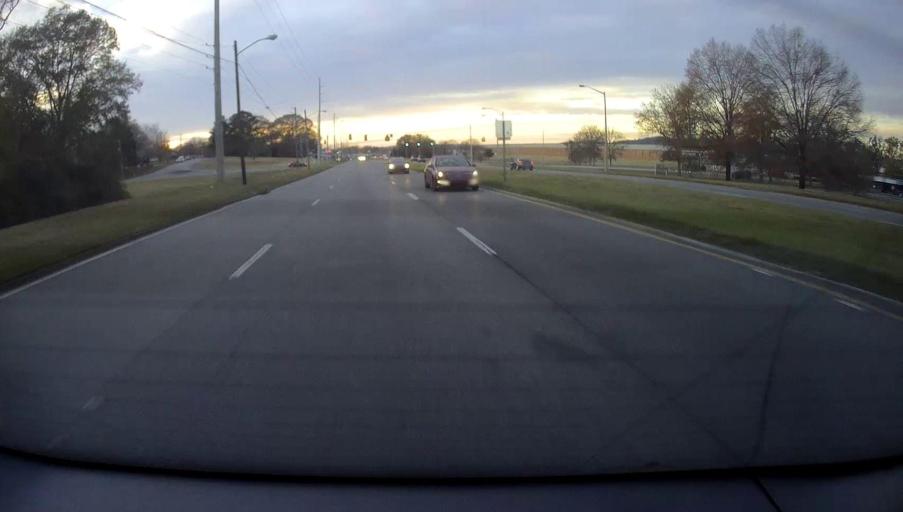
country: US
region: Alabama
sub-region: Etowah County
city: Gadsden
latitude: 34.0068
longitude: -85.9740
